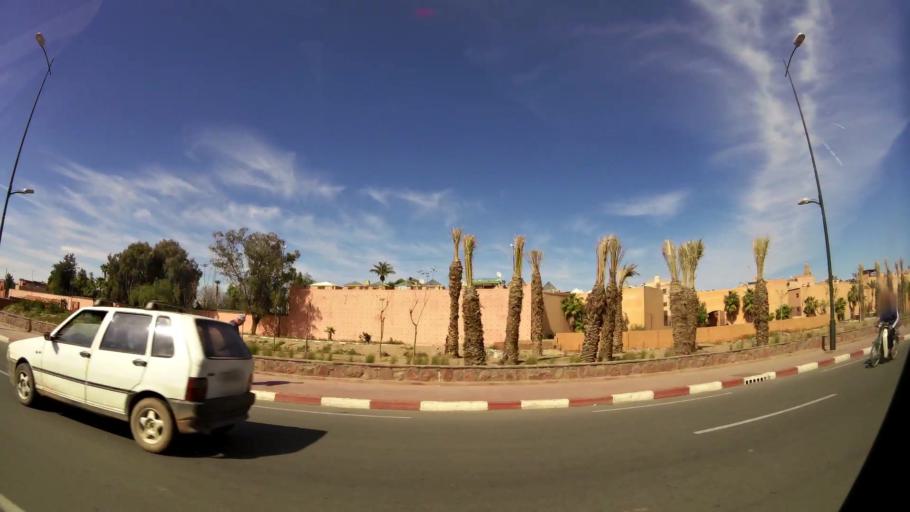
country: MA
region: Marrakech-Tensift-Al Haouz
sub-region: Marrakech
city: Marrakesh
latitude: 31.6392
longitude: -7.9819
